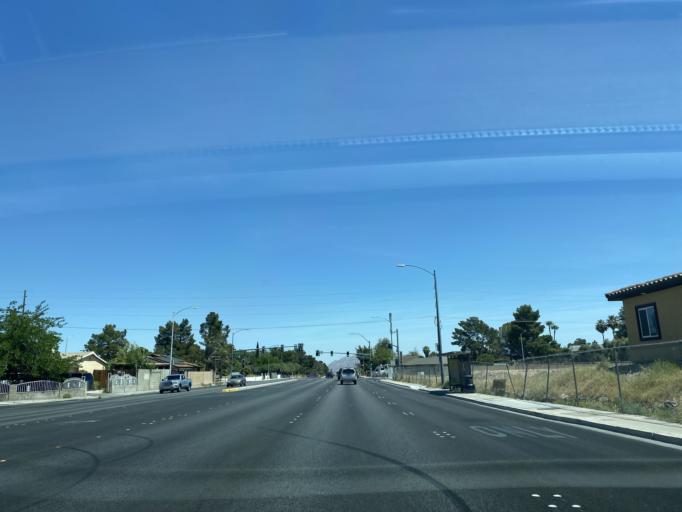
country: US
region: Nevada
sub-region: Clark County
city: Las Vegas
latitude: 36.1956
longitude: -115.2164
